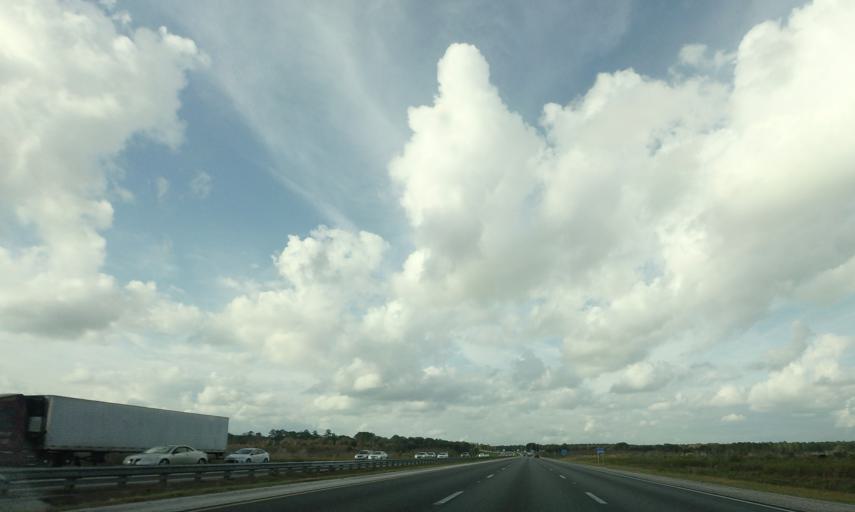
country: US
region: Florida
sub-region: Alachua County
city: Gainesville
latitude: 29.5831
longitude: -82.3583
